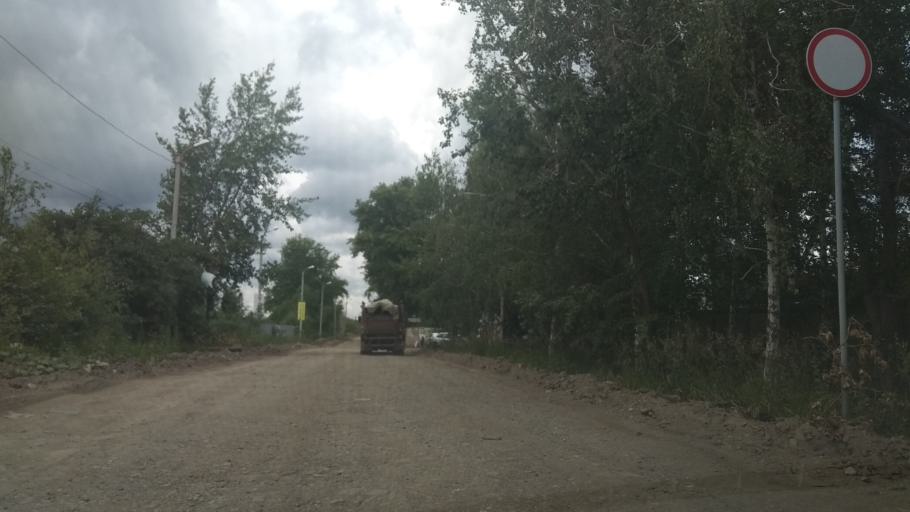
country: RU
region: Sverdlovsk
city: Verkhnyaya Pyshma
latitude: 56.9155
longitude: 60.5771
